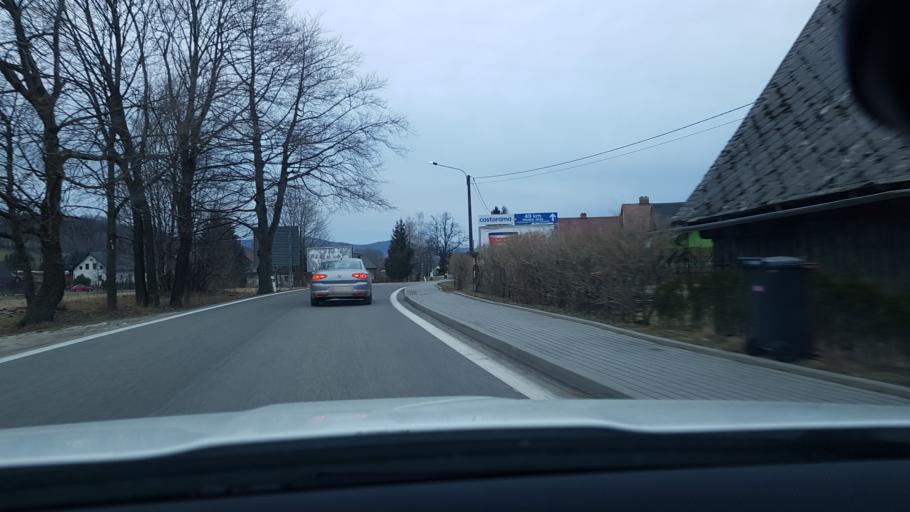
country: CZ
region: Olomoucky
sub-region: Okres Jesenik
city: Jesenik
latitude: 50.1660
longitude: 17.1955
